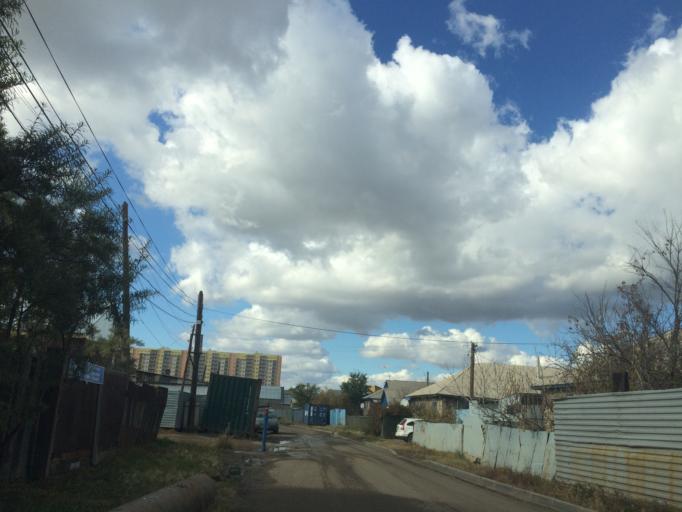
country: KZ
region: Astana Qalasy
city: Astana
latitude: 51.1870
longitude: 71.3892
